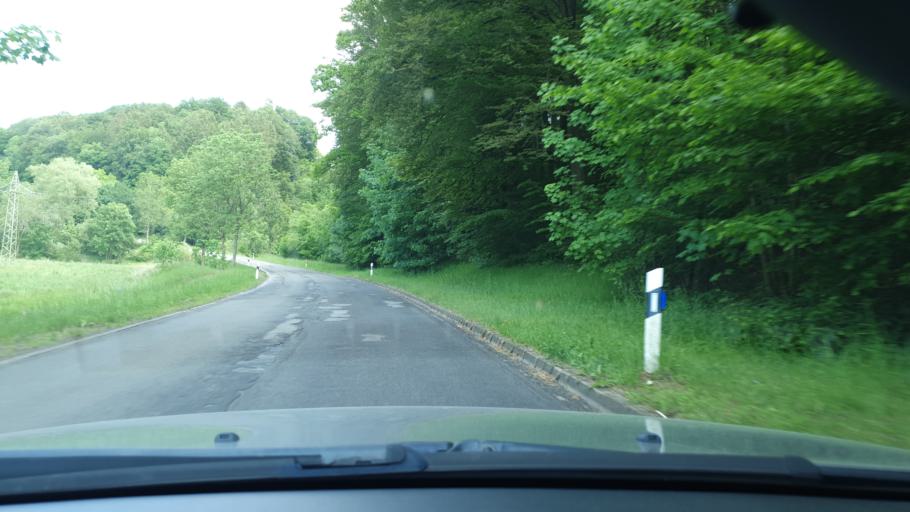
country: DE
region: Rheinland-Pfalz
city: Reifenberg
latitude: 49.2816
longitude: 7.4935
